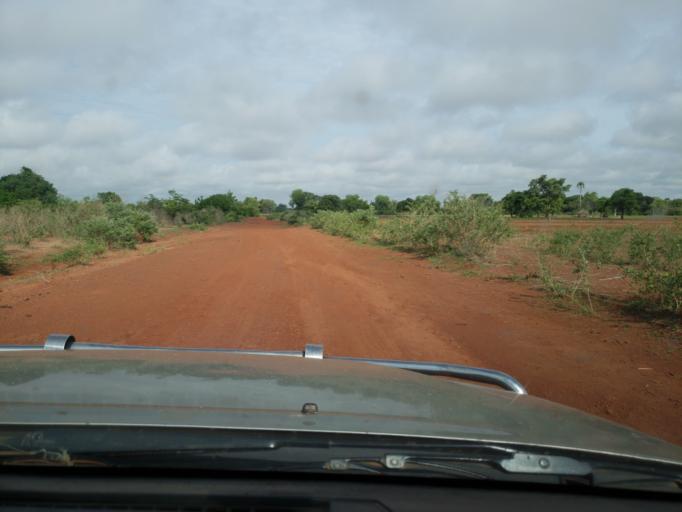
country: ML
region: Sikasso
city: Koutiala
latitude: 12.3929
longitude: -5.9844
